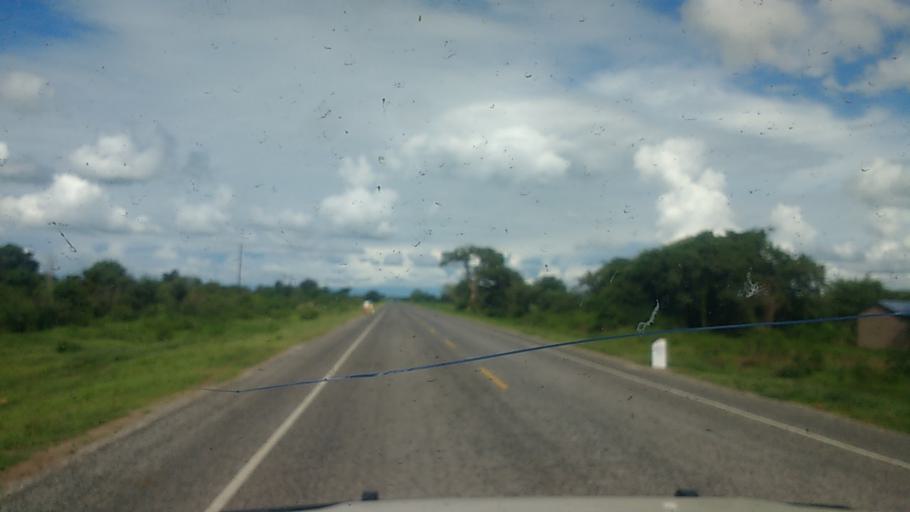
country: UG
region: Eastern Region
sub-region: Katakwi District
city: Katakwi
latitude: 1.9187
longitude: 34.0051
